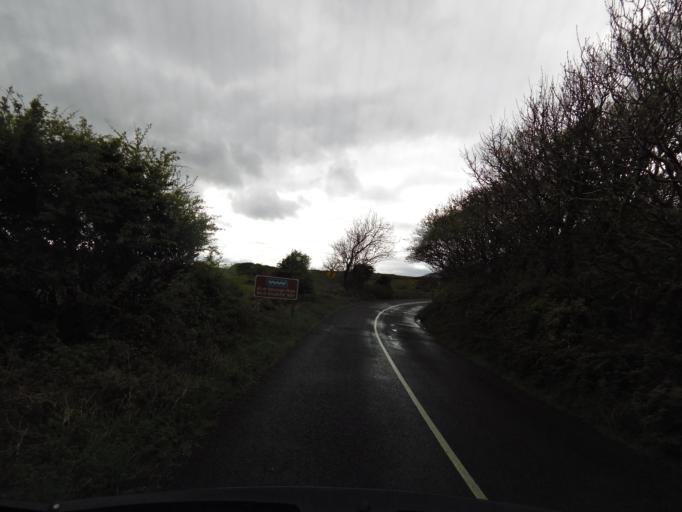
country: IE
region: Connaught
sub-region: County Galway
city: Bearna
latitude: 53.0455
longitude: -9.3394
